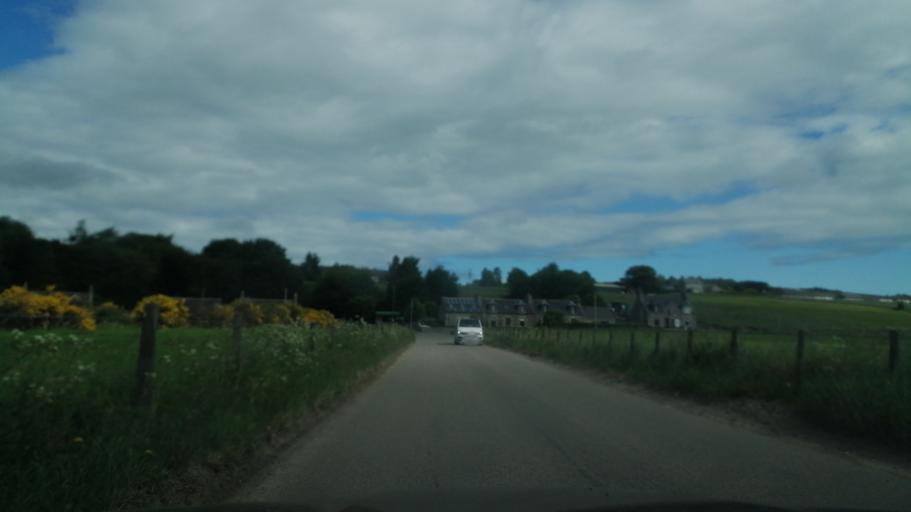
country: GB
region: Scotland
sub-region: Moray
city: Keith
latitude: 57.5545
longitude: -2.9472
